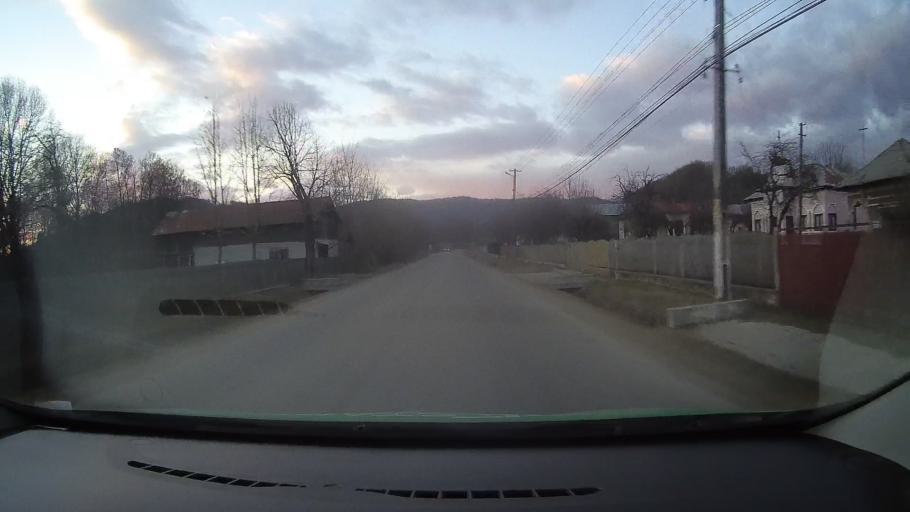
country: RO
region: Dambovita
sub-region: Comuna Valea Lunga
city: Valea Lunga-Cricov
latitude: 45.0677
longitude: 25.5826
